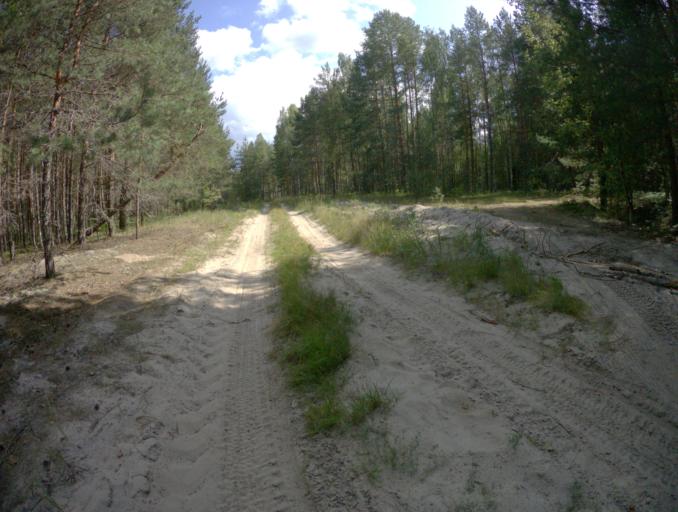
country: RU
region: Vladimir
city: Vorsha
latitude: 55.9181
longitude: 40.1507
